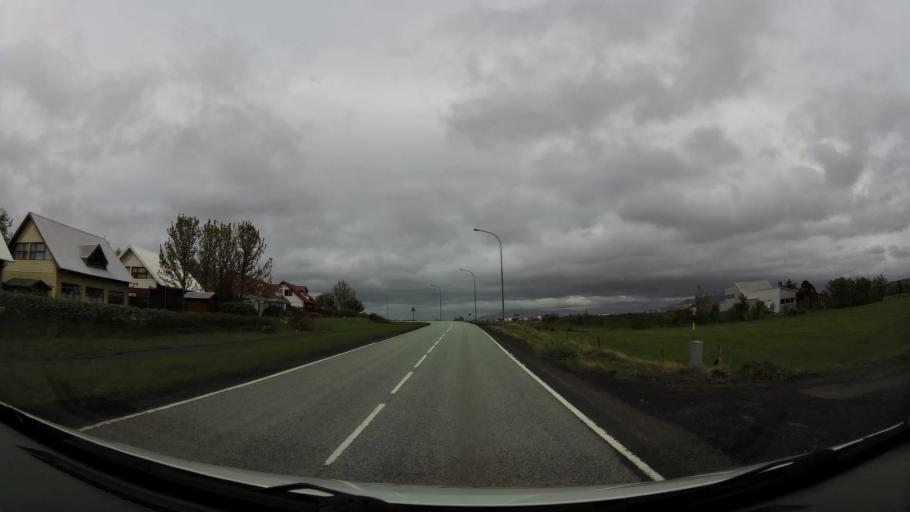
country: IS
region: Capital Region
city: Alftanes
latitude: 64.1068
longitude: -22.0098
